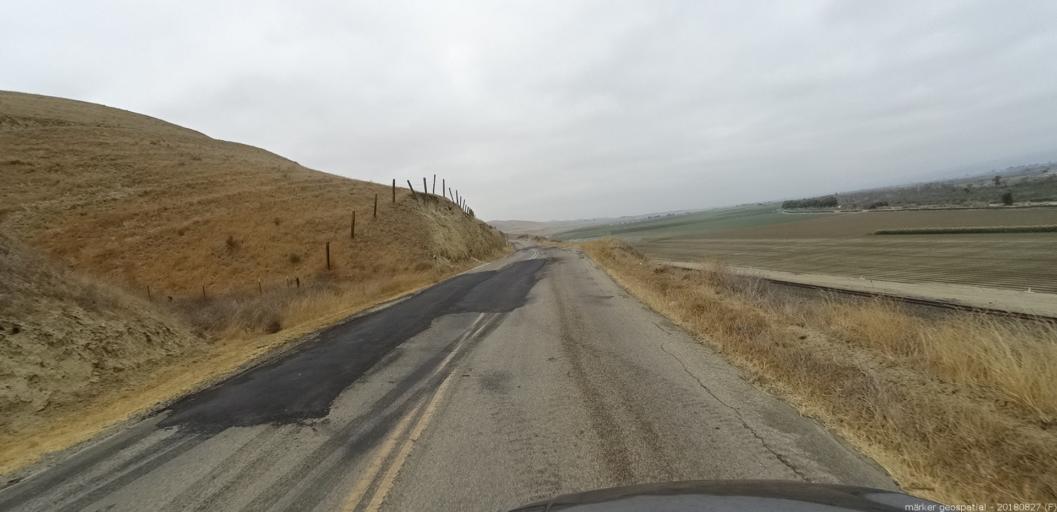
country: US
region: California
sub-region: Monterey County
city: Greenfield
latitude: 36.3195
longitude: -121.1785
